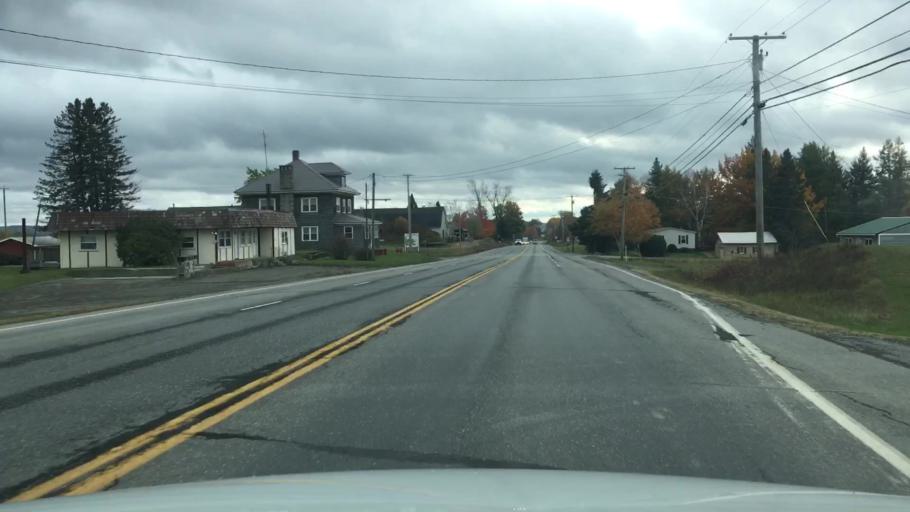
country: US
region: Maine
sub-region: Aroostook County
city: Houlton
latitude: 46.2181
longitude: -67.8410
